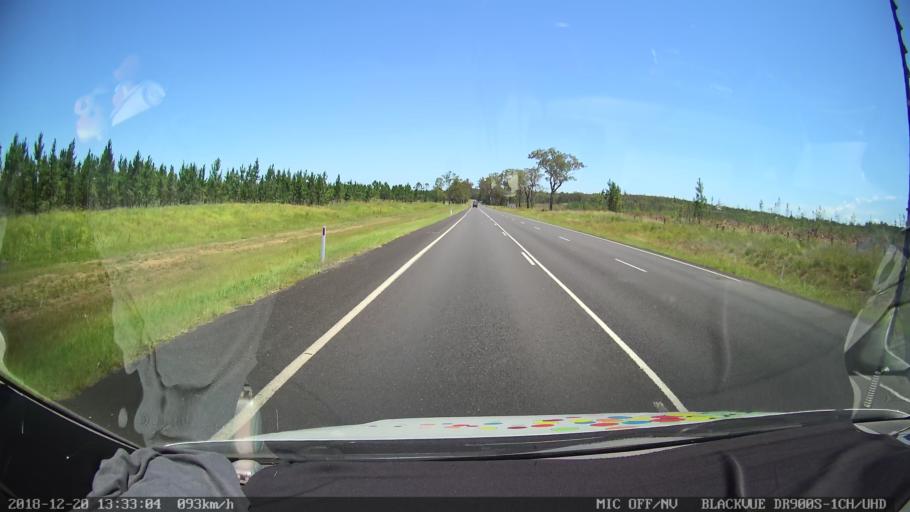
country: AU
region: New South Wales
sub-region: Clarence Valley
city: Gordon
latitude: -29.2403
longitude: 152.9879
